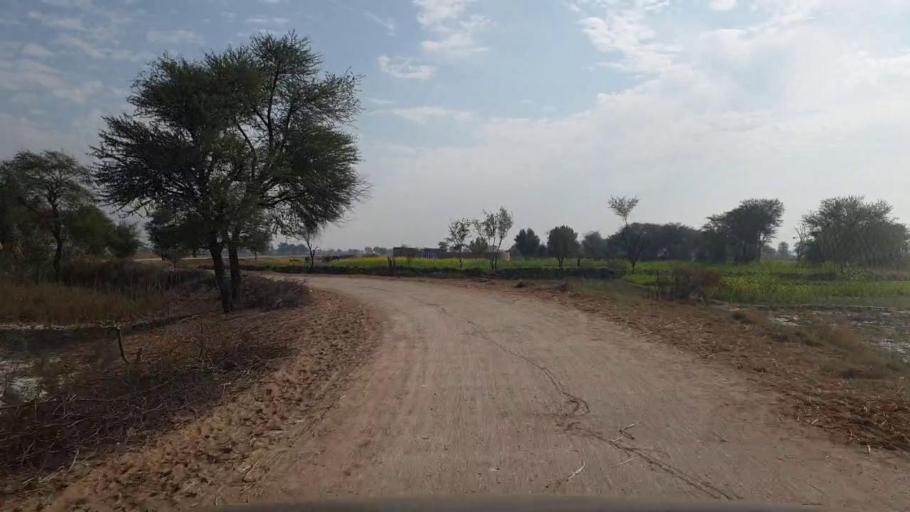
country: PK
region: Sindh
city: Hala
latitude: 25.9933
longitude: 68.4260
